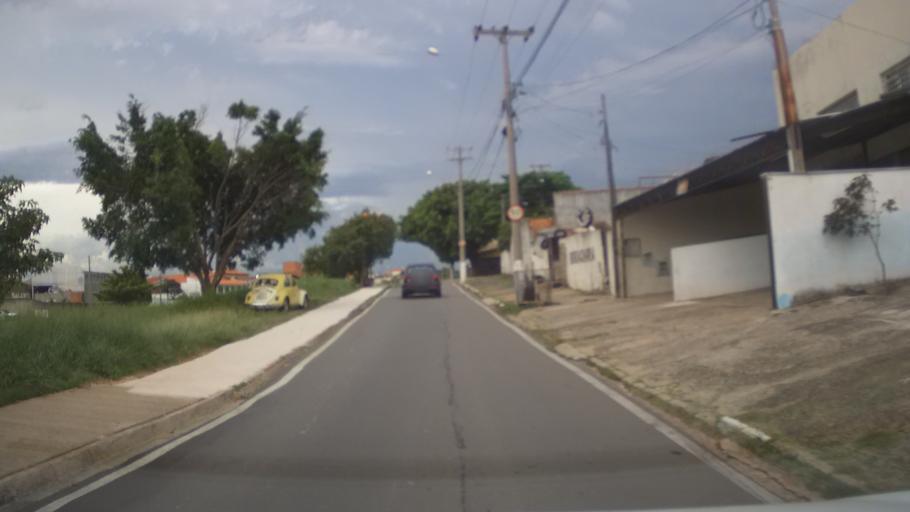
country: BR
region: Sao Paulo
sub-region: Campinas
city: Campinas
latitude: -22.9318
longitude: -47.1124
